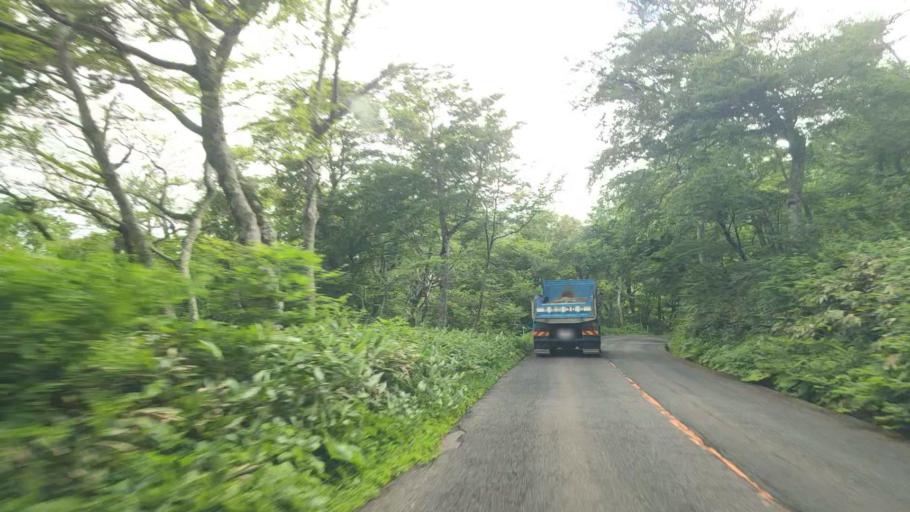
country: JP
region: Tottori
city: Yonago
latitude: 35.3857
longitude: 133.5263
